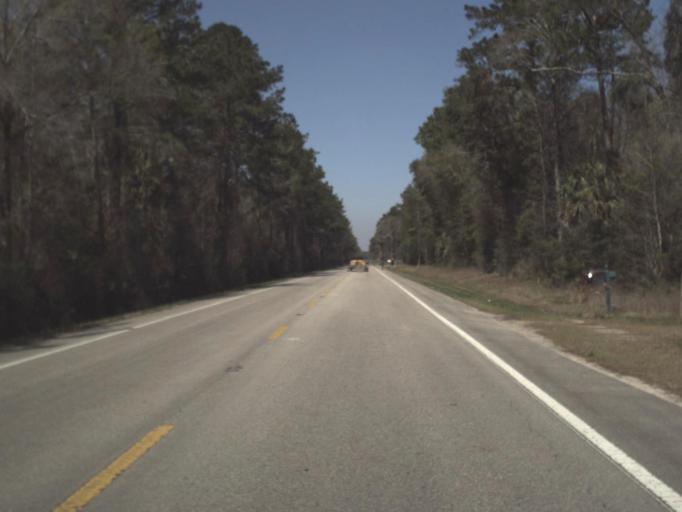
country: US
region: Florida
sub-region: Leon County
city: Woodville
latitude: 30.2067
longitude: -84.2211
